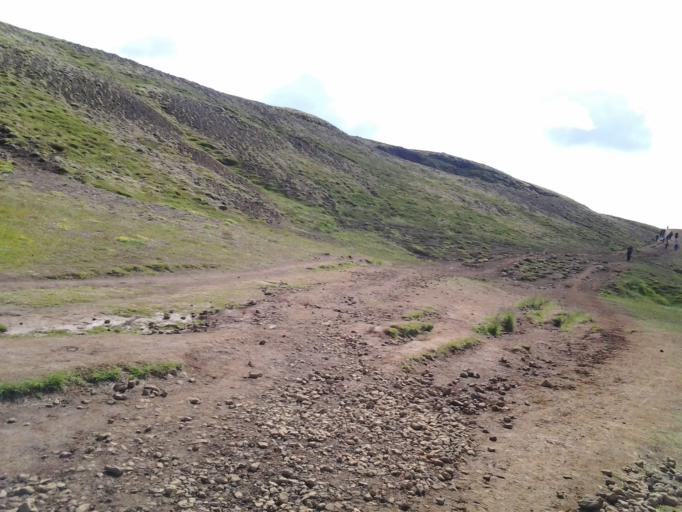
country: IS
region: South
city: Hveragerdi
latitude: 64.0384
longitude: -21.2185
